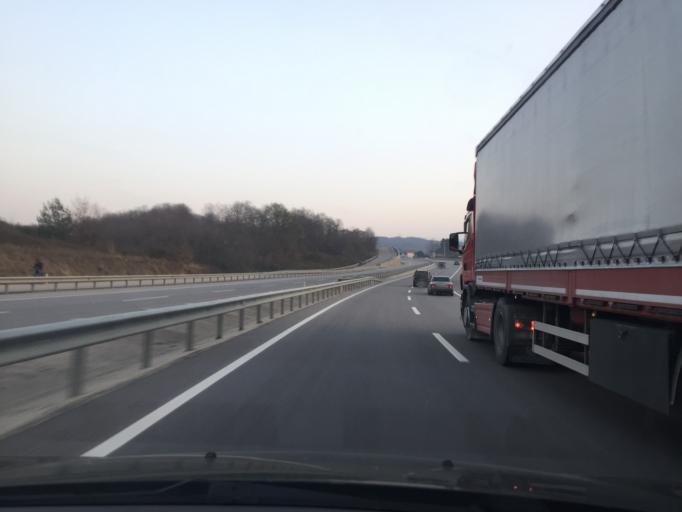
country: TR
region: Sakarya
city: Akyazi
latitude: 40.6292
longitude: 30.6416
